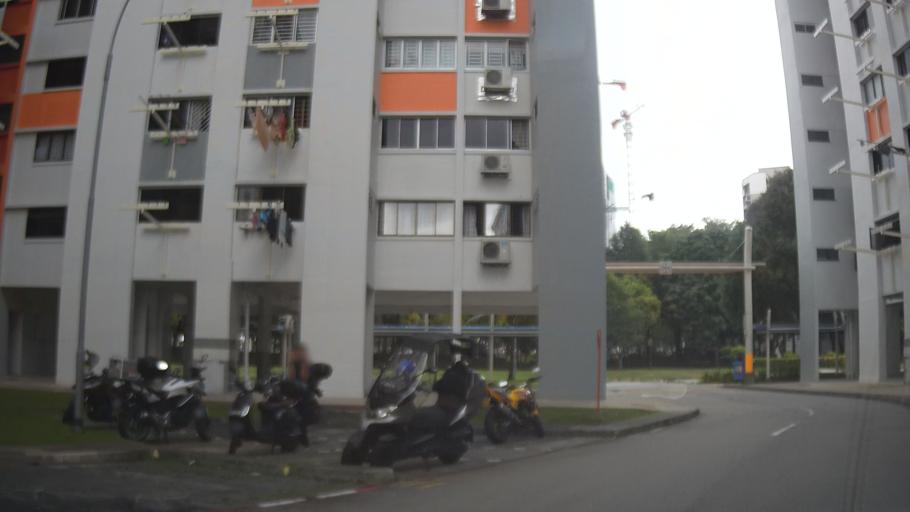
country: MY
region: Johor
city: Johor Bahru
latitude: 1.4337
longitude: 103.7824
